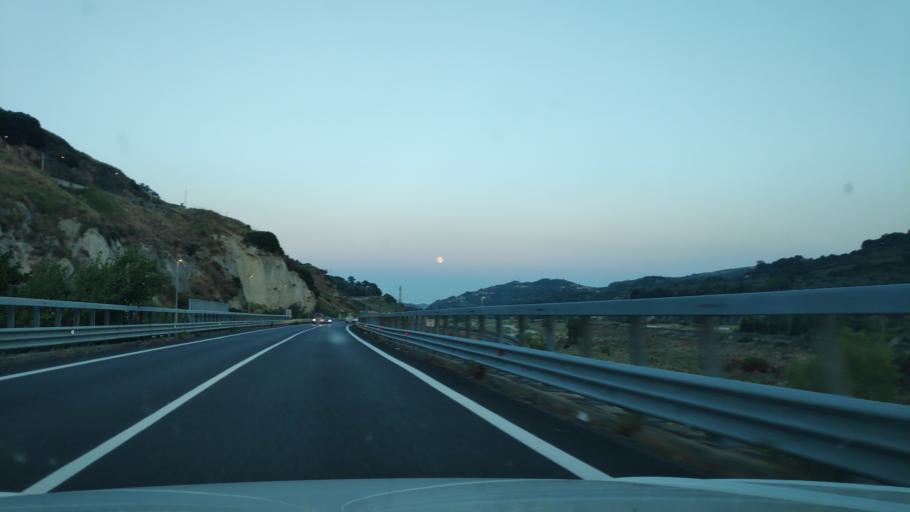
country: IT
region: Calabria
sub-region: Provincia di Reggio Calabria
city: Mammola
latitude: 38.3564
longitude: 16.2389
